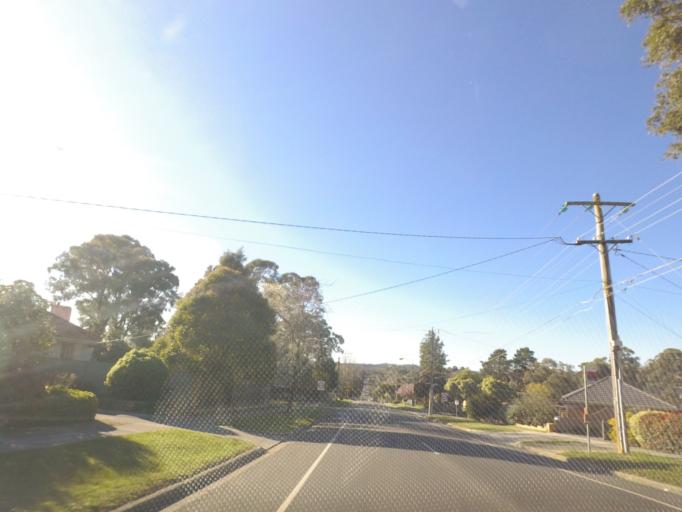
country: AU
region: Victoria
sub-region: Yarra Ranges
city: Kilsyth
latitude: -37.7988
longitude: 145.3130
